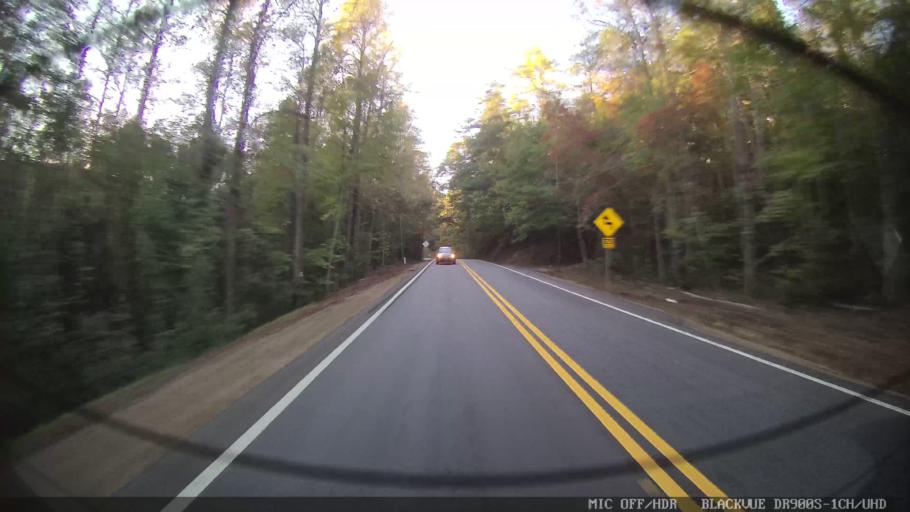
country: US
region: Georgia
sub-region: Lumpkin County
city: Dahlonega
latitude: 34.6266
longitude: -83.9485
